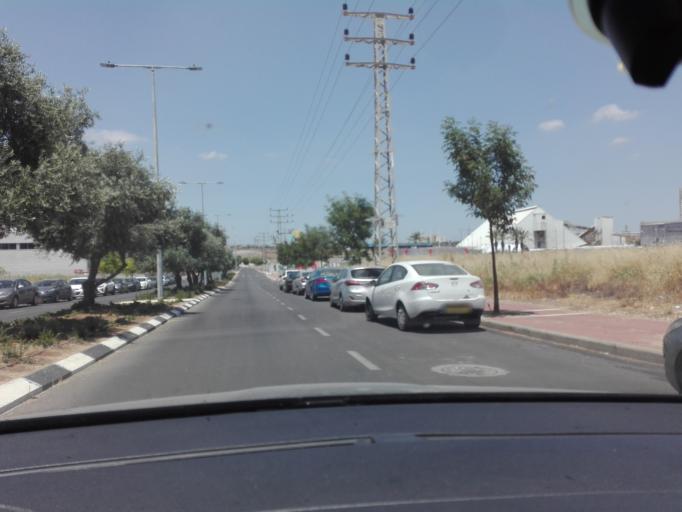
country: IL
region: Southern District
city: Qiryat Gat
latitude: 31.5951
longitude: 34.7834
